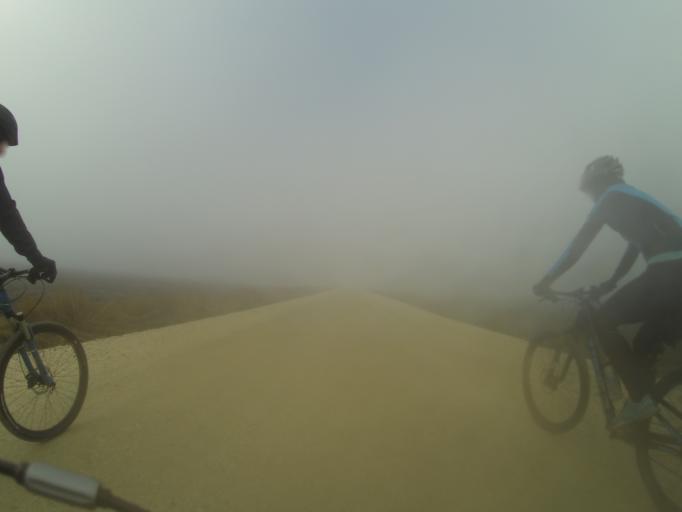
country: RO
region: Mehedinti
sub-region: Comuna Baclesu
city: Baclesu
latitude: 44.4549
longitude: 23.1183
